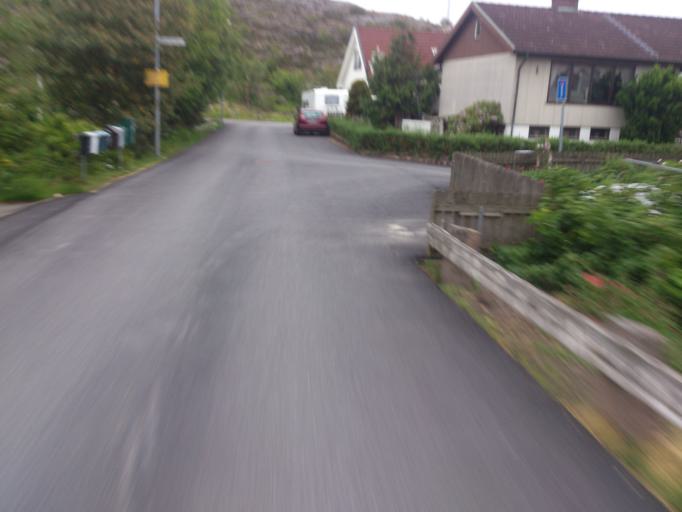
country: SE
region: Vaestra Goetaland
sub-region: Sotenas Kommun
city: Kungshamn
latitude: 58.3814
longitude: 11.2691
